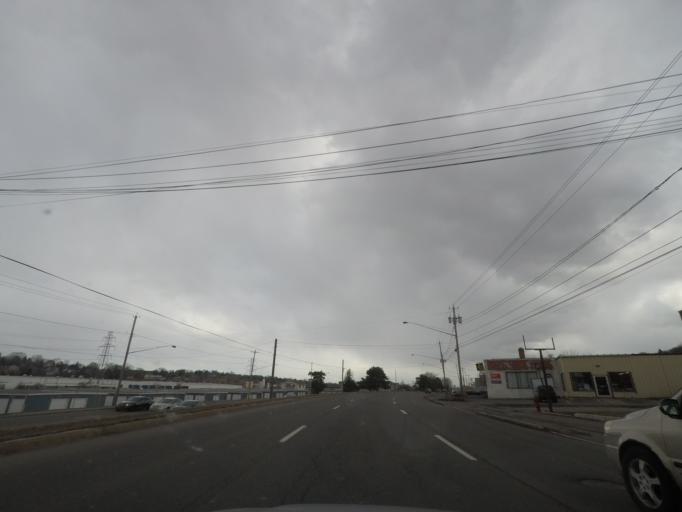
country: US
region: New York
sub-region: Onondaga County
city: Lyncourt
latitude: 43.0525
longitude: -76.1109
